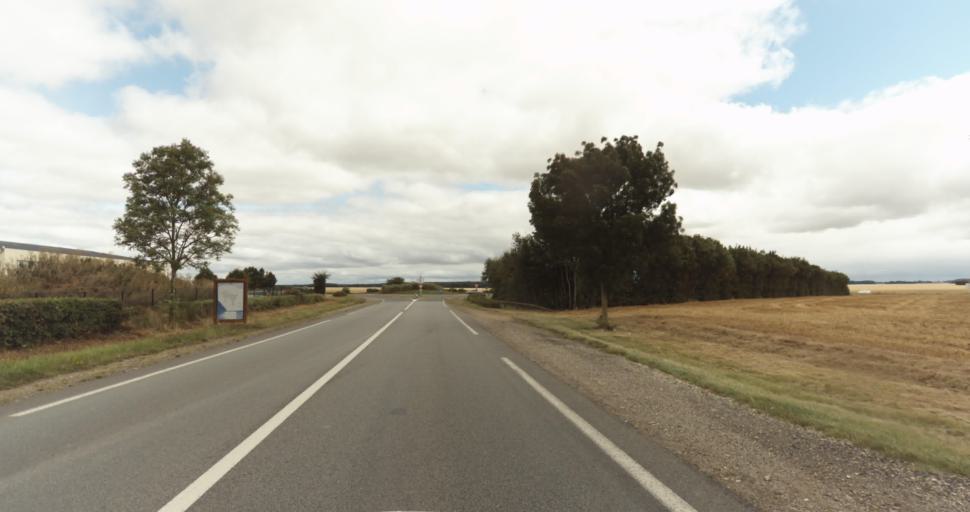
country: FR
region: Haute-Normandie
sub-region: Departement de l'Eure
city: Evreux
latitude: 48.9546
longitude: 1.2193
